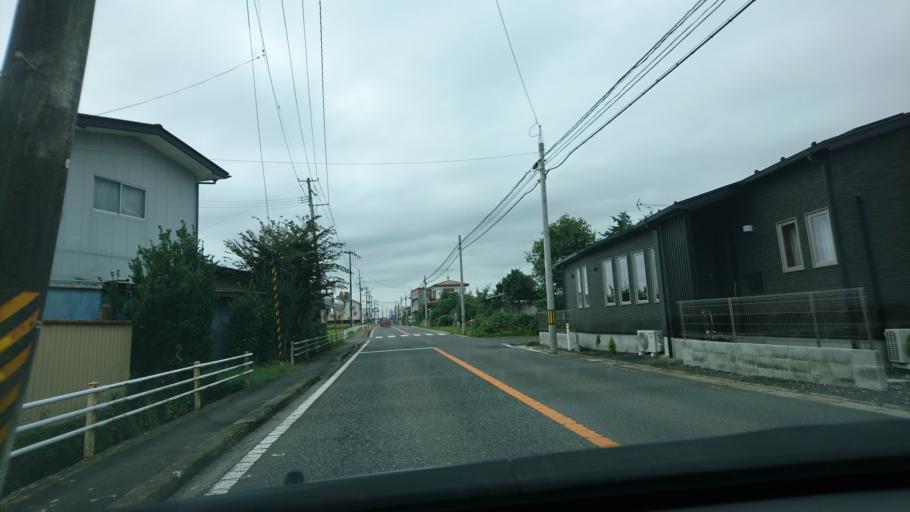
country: JP
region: Iwate
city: Ichinoseki
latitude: 38.7515
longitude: 141.0575
